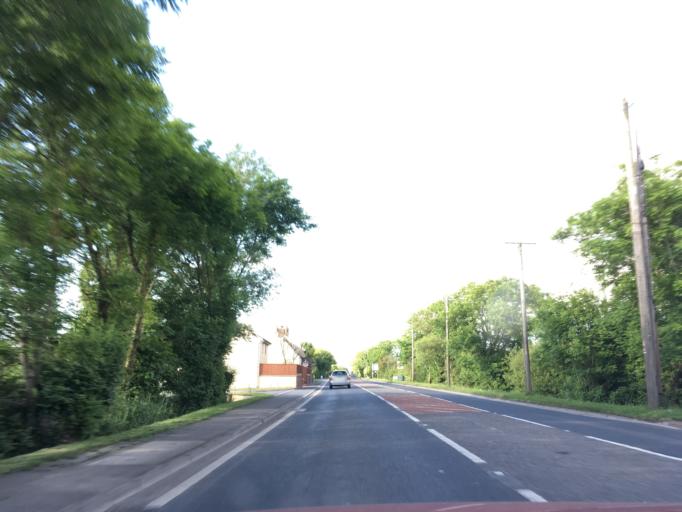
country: GB
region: England
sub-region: Somerset
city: Highbridge
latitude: 51.2317
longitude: -2.9587
